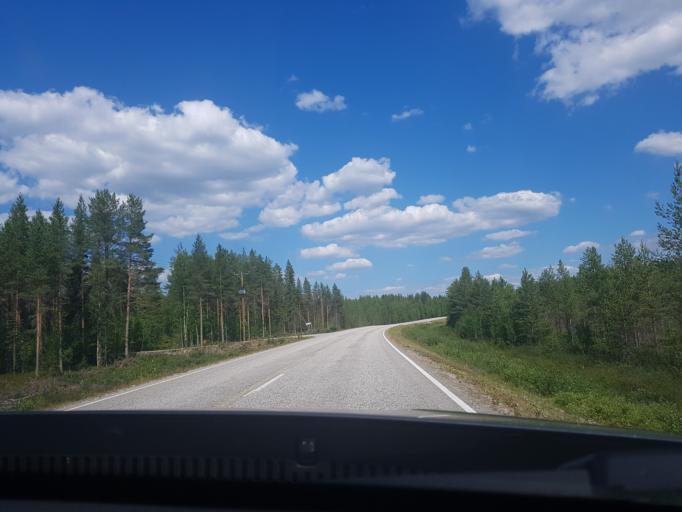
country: FI
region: Kainuu
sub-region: Kehys-Kainuu
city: Kuhmo
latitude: 64.2232
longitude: 29.8016
